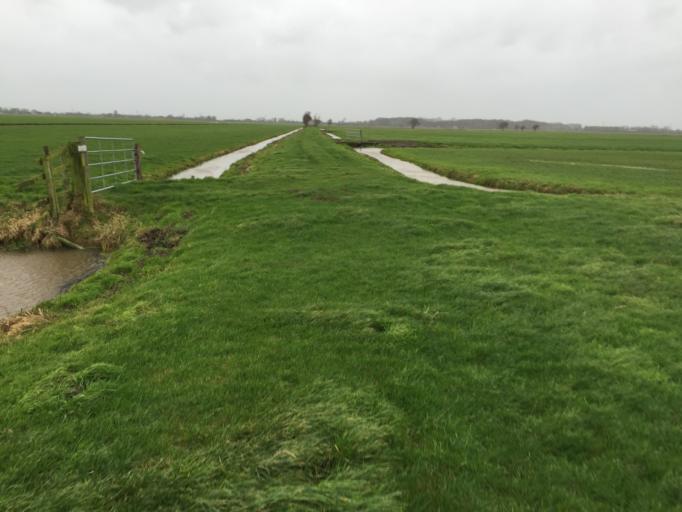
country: NL
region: Utrecht
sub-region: Gemeente Montfoort
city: Montfoort
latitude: 52.0390
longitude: 4.9211
